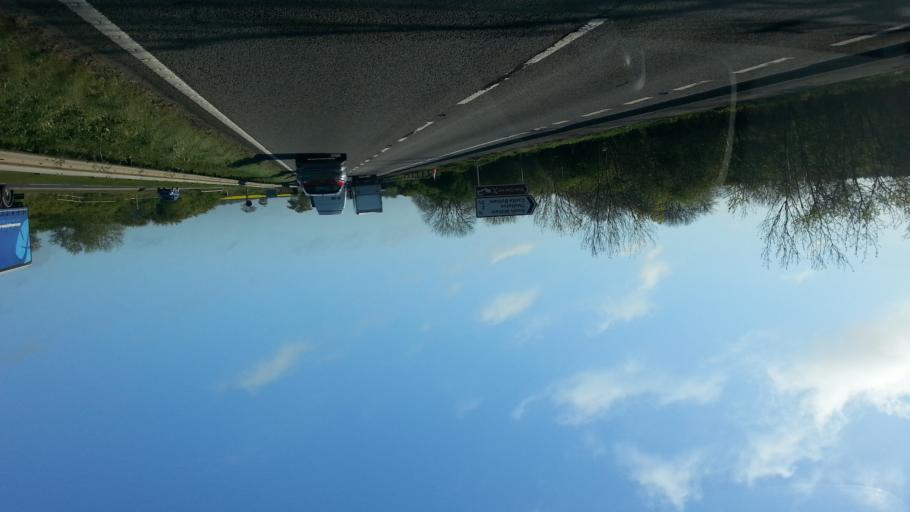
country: GB
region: England
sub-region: District of Rutland
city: Greetham
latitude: 52.7634
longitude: -0.6106
